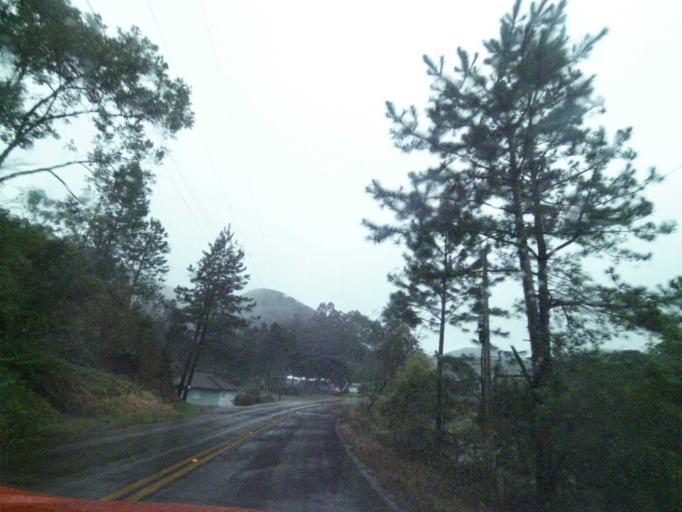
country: BR
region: Santa Catarina
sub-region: Anitapolis
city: Anitapolis
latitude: -27.8423
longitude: -49.0515
